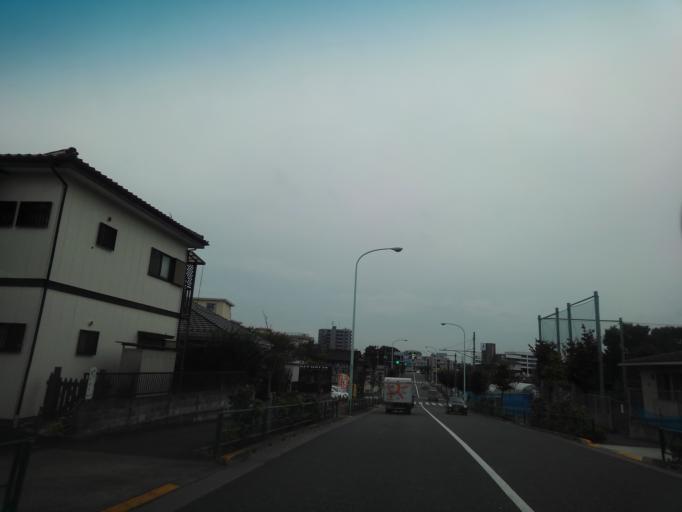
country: JP
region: Tokyo
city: Higashimurayama-shi
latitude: 35.7505
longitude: 139.4158
